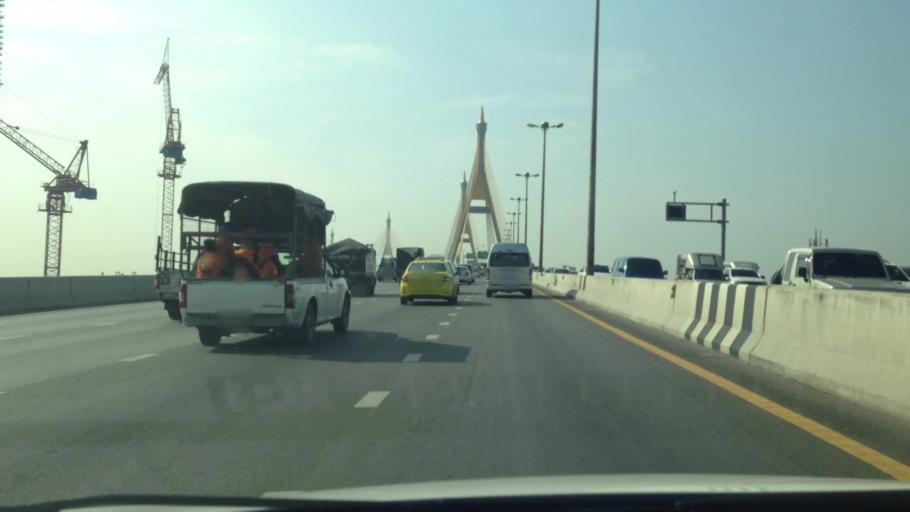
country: TH
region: Samut Prakan
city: Phra Pradaeng
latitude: 13.6765
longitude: 100.5393
